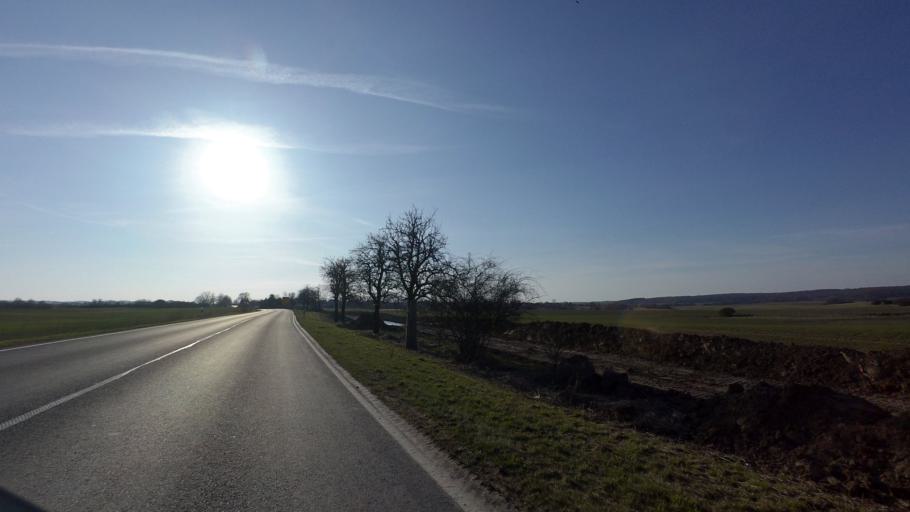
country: DE
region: Brandenburg
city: Chorin
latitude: 52.9562
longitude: 13.9068
